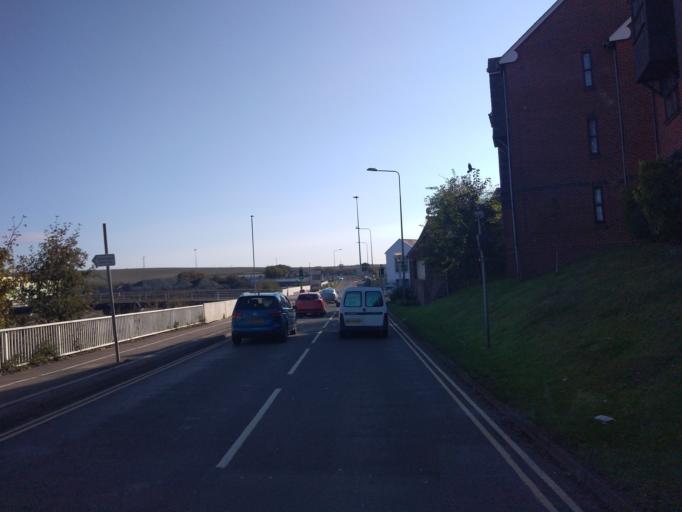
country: GB
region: England
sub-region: East Sussex
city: Newhaven
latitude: 50.7951
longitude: 0.0487
